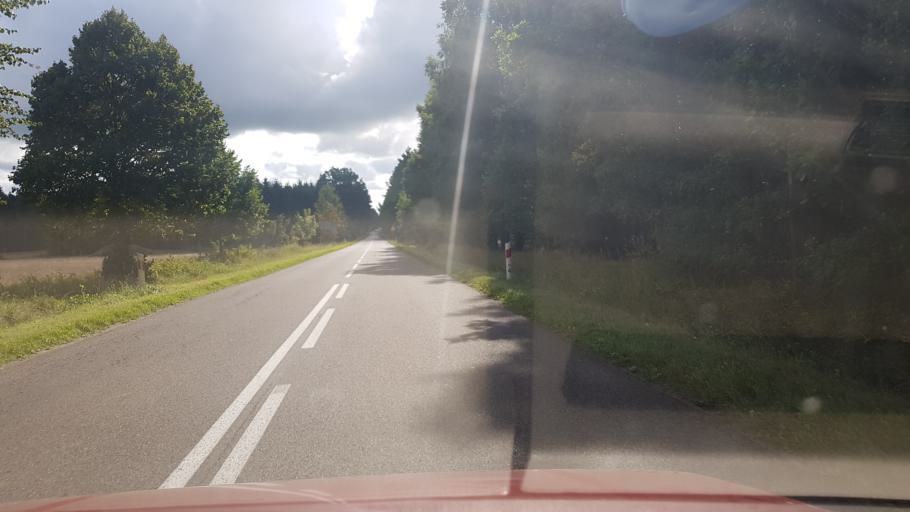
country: PL
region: West Pomeranian Voivodeship
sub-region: Powiat koszalinski
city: Polanow
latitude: 54.1060
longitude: 16.7962
